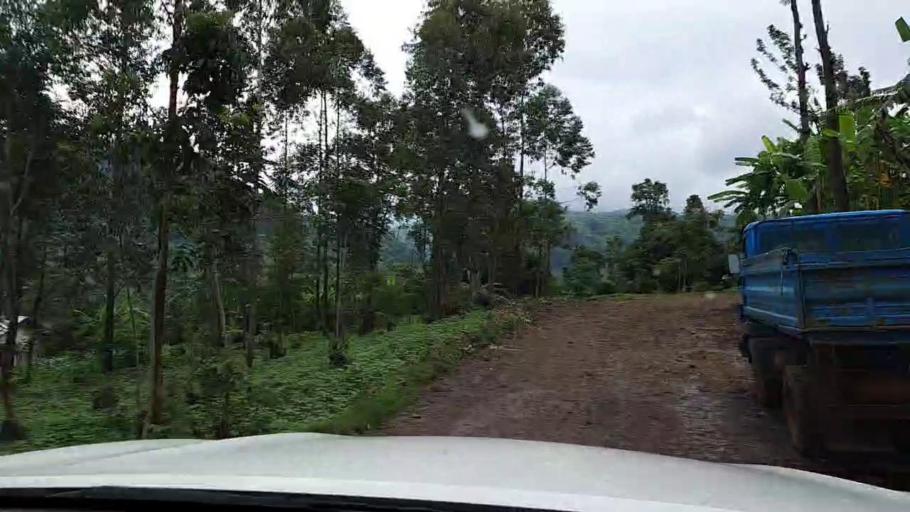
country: RW
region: Western Province
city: Cyangugu
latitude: -2.5481
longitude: 29.0381
